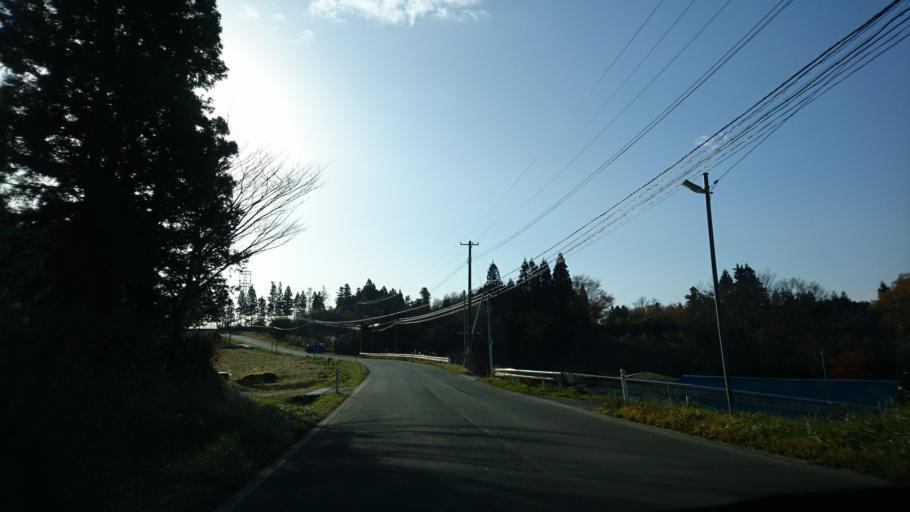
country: JP
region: Iwate
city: Ichinoseki
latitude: 38.8774
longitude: 141.2917
